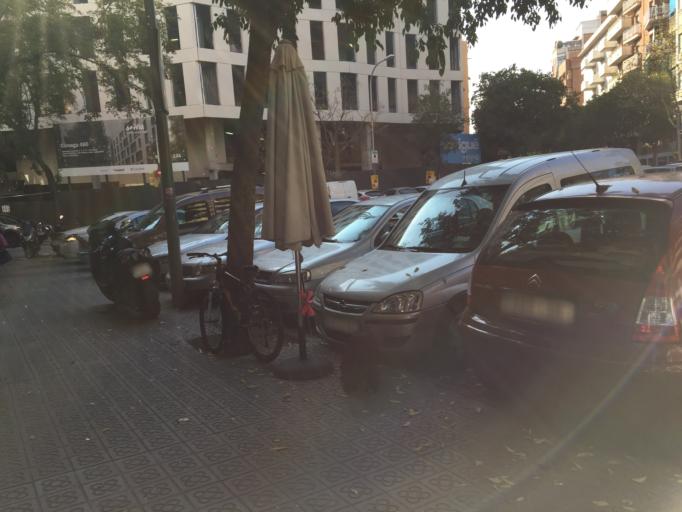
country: ES
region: Catalonia
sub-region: Provincia de Barcelona
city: Gracia
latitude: 41.4046
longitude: 2.1700
